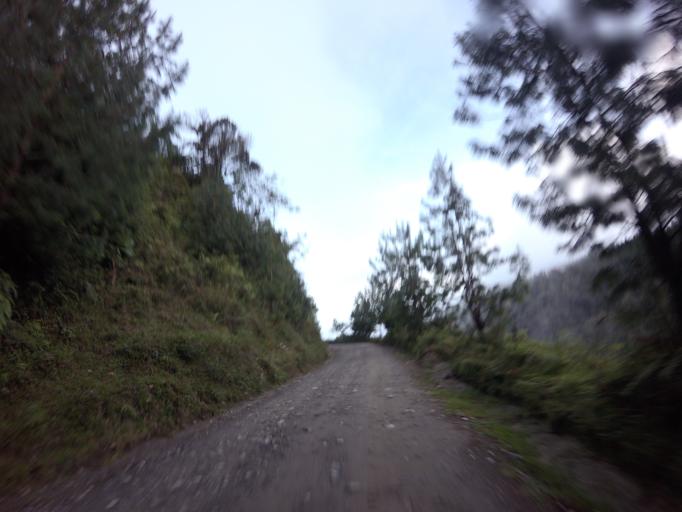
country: CO
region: Caldas
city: Pensilvania
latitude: 5.4170
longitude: -75.1299
